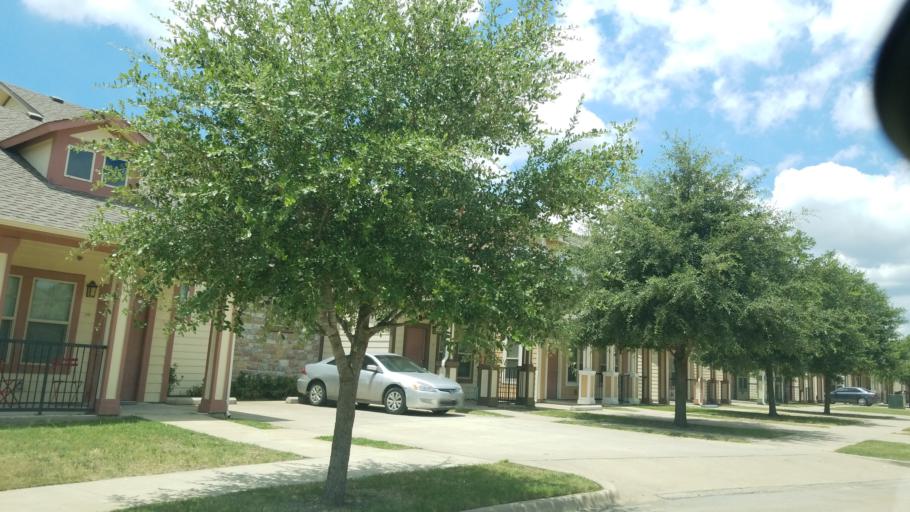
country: US
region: Texas
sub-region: Dallas County
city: Dallas
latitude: 32.7340
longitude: -96.7550
